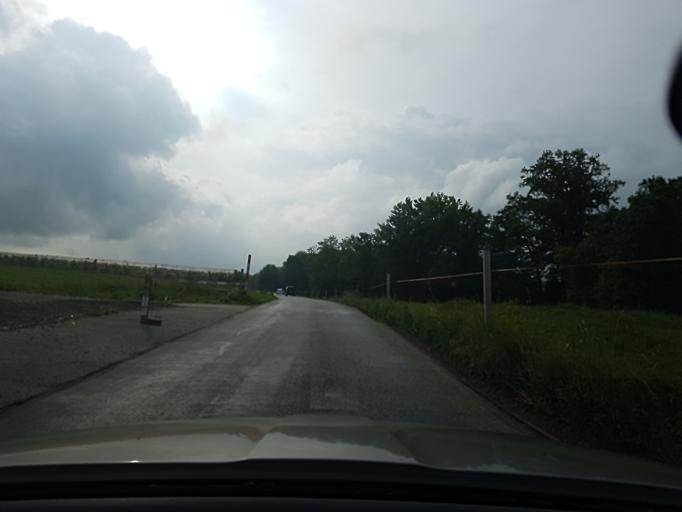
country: CH
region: Thurgau
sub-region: Arbon District
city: Roggwil
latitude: 47.5143
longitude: 9.3692
